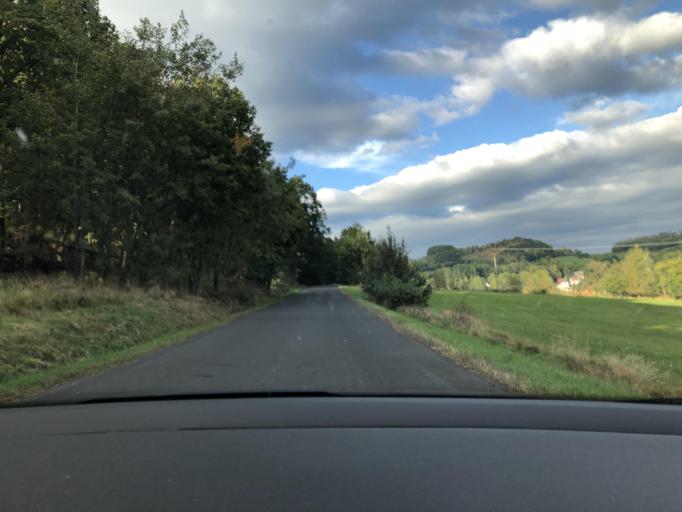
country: CZ
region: Ustecky
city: Zitenice
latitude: 50.5999
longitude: 14.1646
